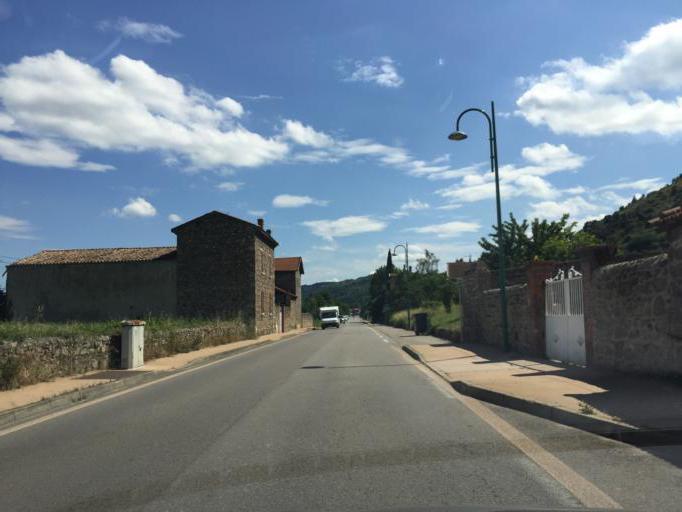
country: FR
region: Rhone-Alpes
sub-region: Departement de l'Ardeche
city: Sarras
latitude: 45.1984
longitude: 4.8014
